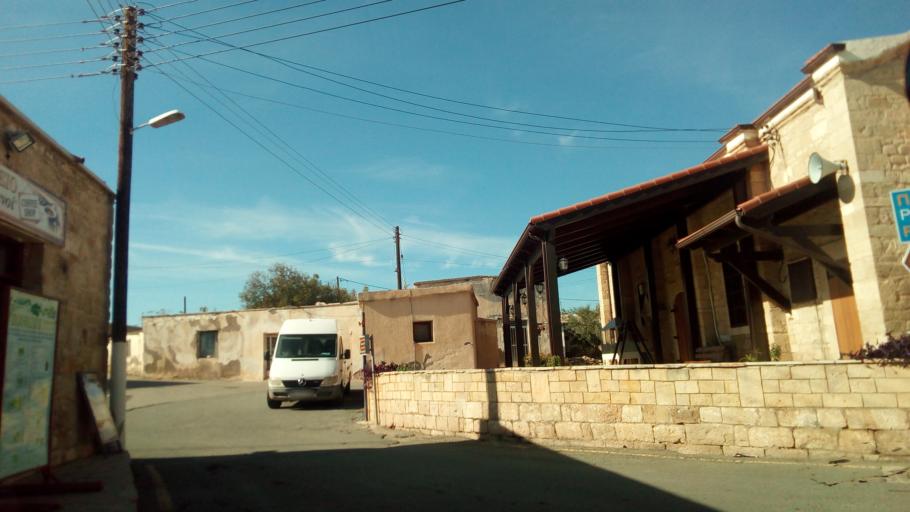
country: CY
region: Limassol
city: Pissouri
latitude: 34.7085
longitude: 32.5750
